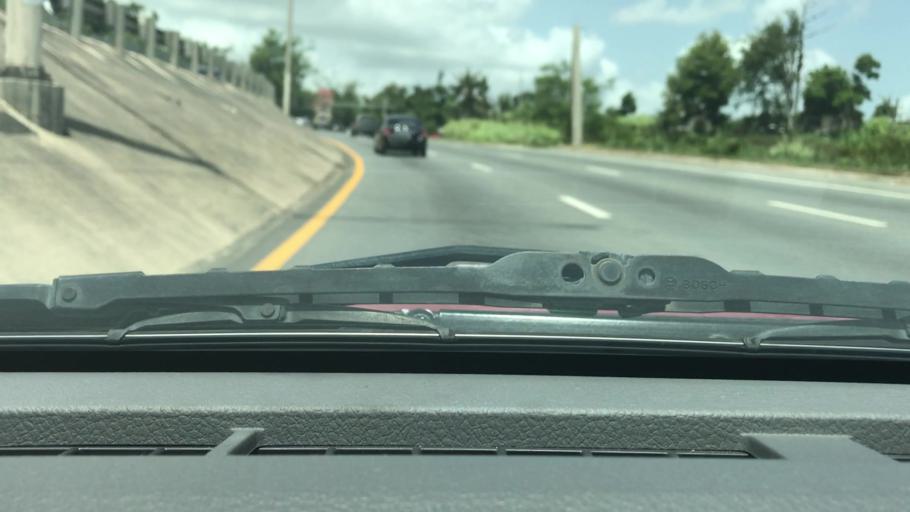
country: PR
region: Toa Alta
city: Pajaros
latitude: 18.3644
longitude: -66.1843
